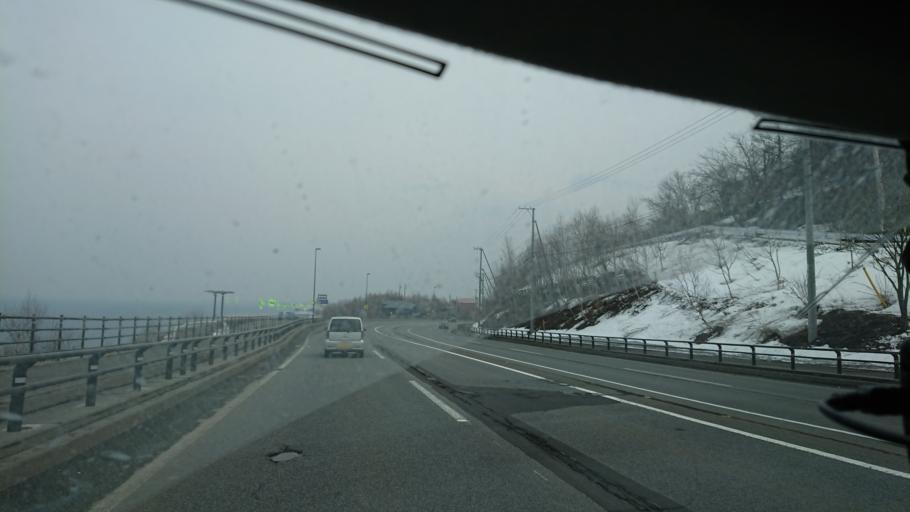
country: JP
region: Hokkaido
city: Otaru
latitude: 43.1508
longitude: 141.1307
